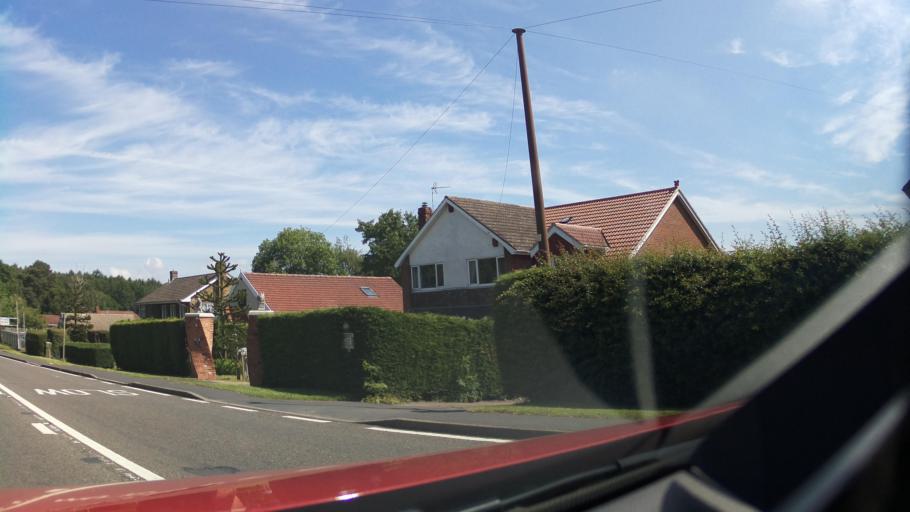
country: GB
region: England
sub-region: North Lincolnshire
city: Manton
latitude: 53.5337
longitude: -0.5772
